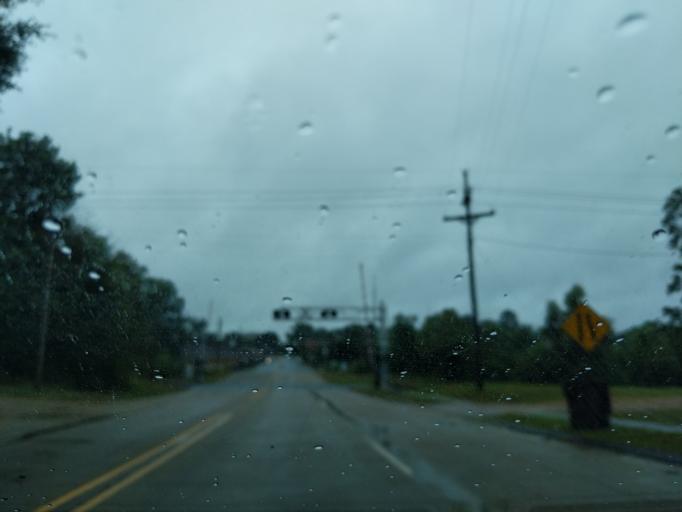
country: US
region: Louisiana
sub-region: Bienville Parish
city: Arcadia
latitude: 32.5477
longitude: -93.0530
